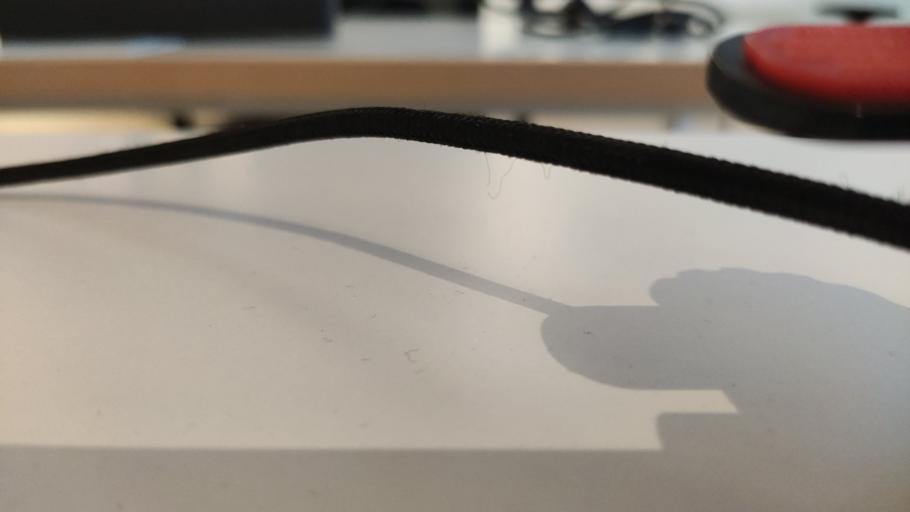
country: RU
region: Moskovskaya
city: Sychevo
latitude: 55.8517
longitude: 36.3609
